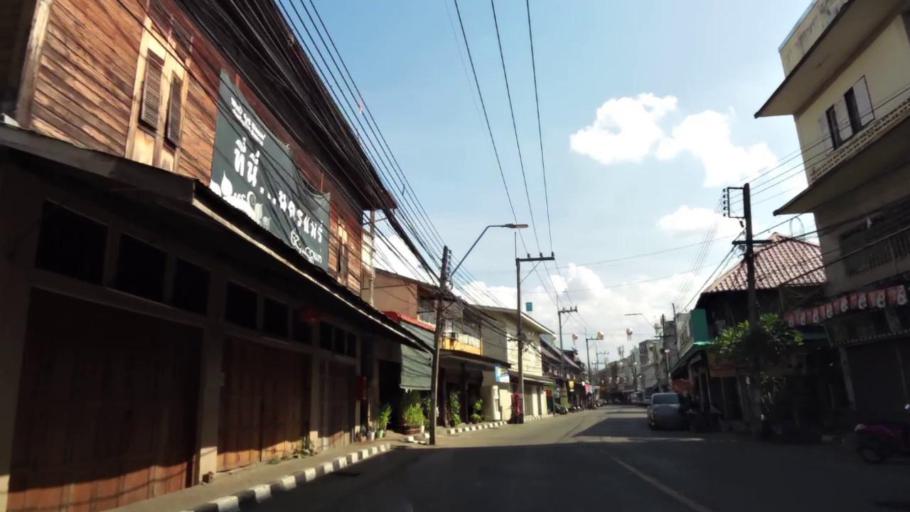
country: TH
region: Phrae
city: Phrae
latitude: 18.1414
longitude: 100.1431
